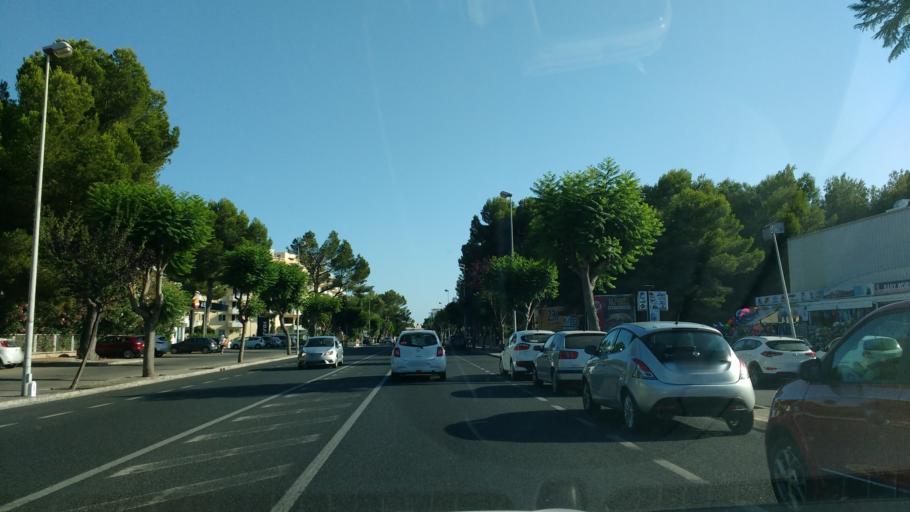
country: ES
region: Balearic Islands
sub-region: Illes Balears
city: Port d'Alcudia
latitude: 39.8215
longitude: 3.1147
